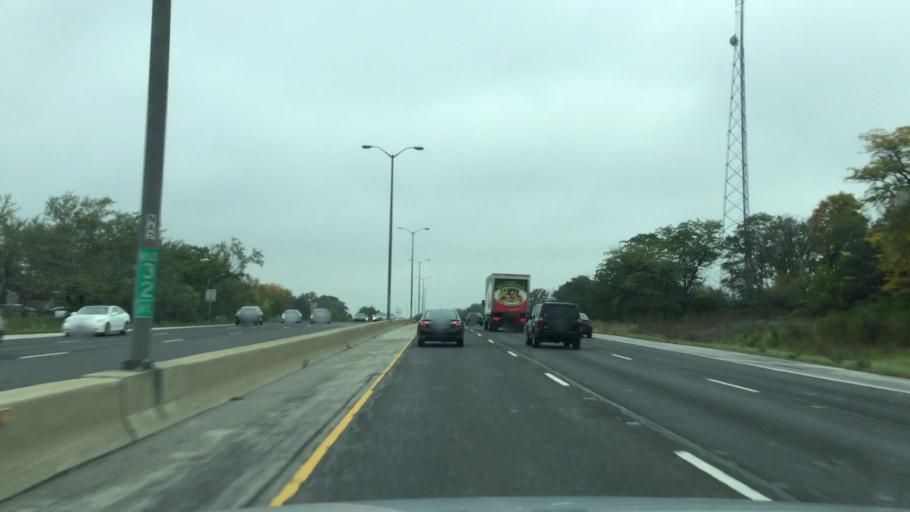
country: US
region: Illinois
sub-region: Cook County
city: Northfield
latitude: 42.1024
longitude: -87.7683
